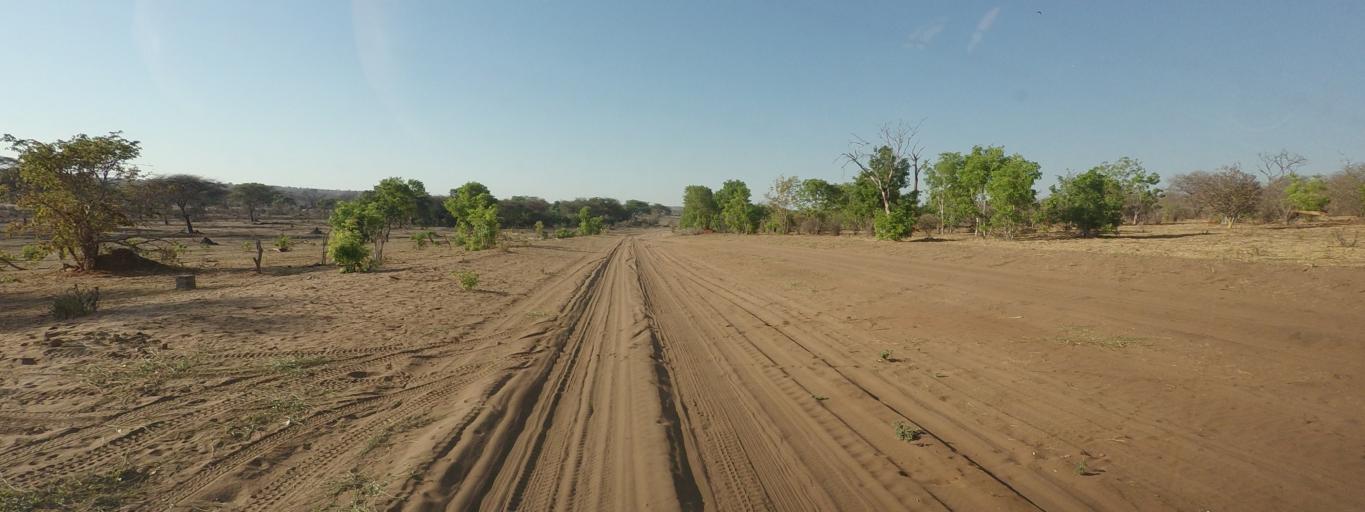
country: BW
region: North West
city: Kasane
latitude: -17.8774
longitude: 25.2344
